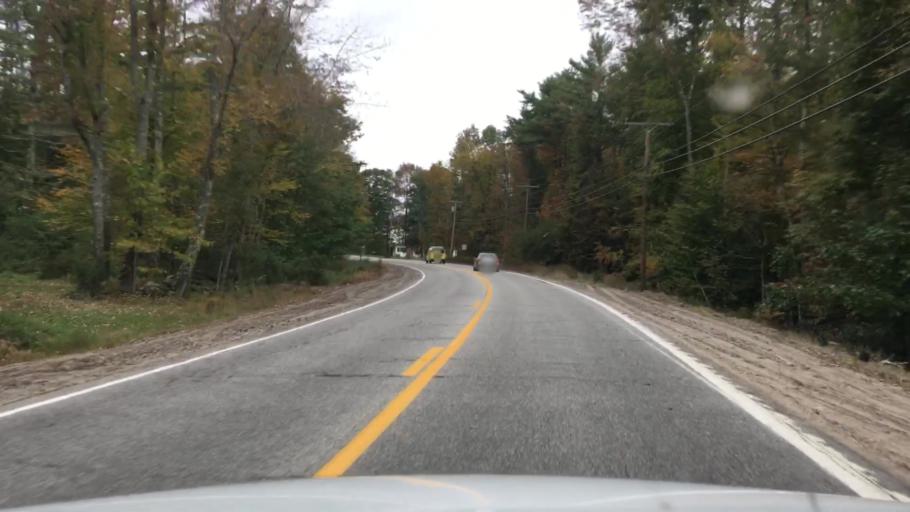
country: US
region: Maine
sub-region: Oxford County
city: Norway
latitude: 44.2197
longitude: -70.5858
